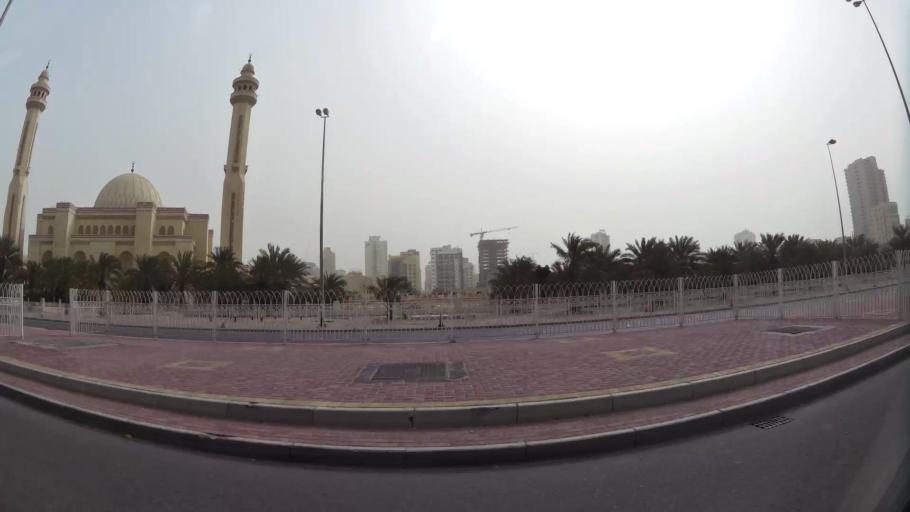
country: BH
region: Manama
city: Manama
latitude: 26.2179
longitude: 50.5971
